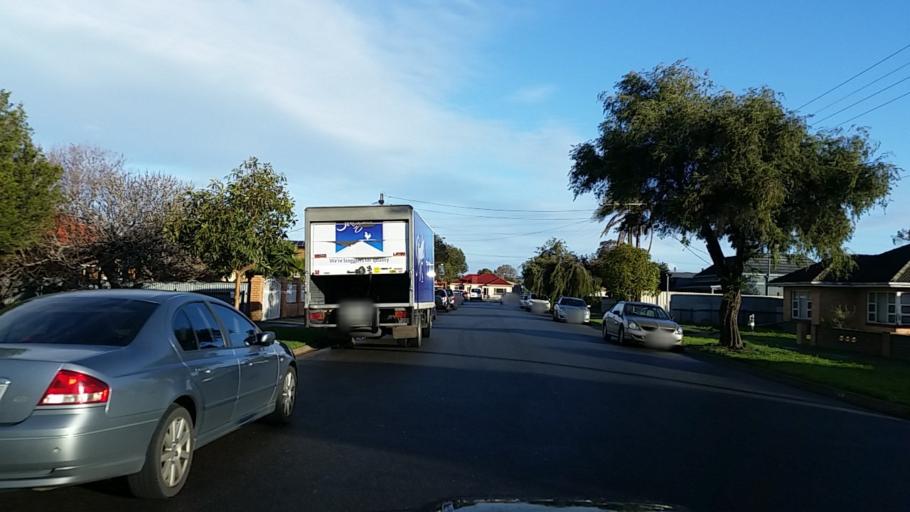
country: AU
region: South Australia
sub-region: Charles Sturt
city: Findon
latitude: -34.9039
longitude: 138.5371
